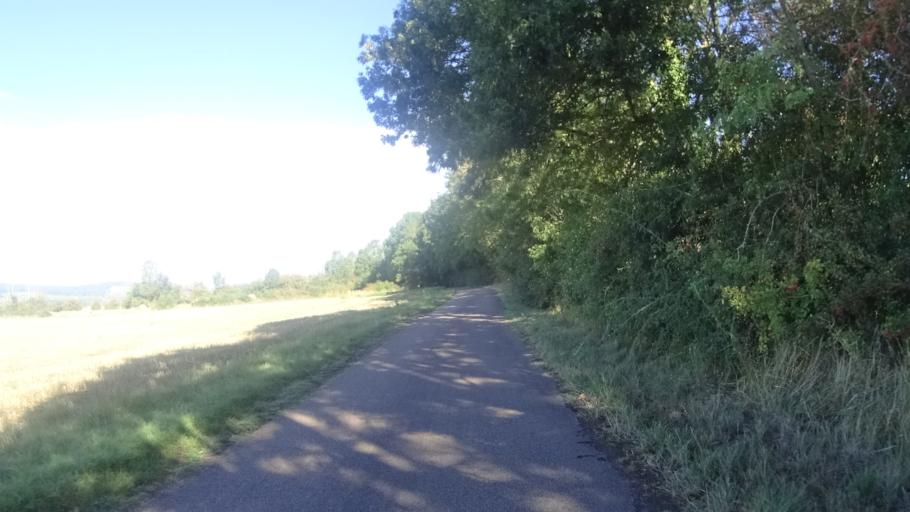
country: FR
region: Centre
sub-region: Departement du Cher
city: Sancerre
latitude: 47.3081
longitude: 2.8947
